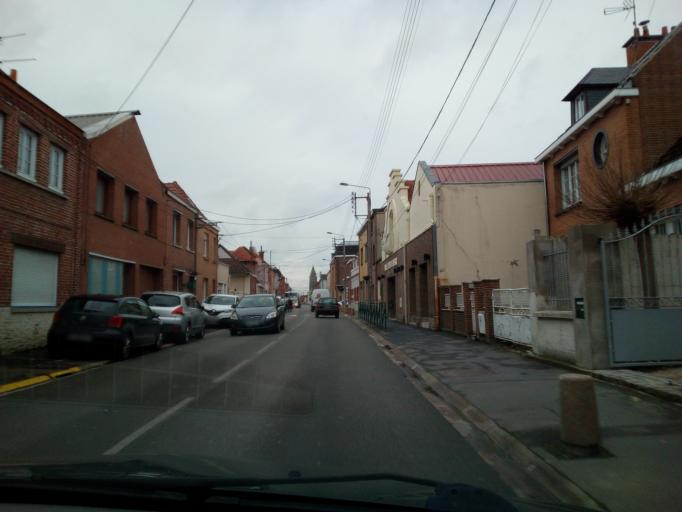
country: FR
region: Nord-Pas-de-Calais
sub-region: Departement du Nord
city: Bauvin
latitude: 50.5139
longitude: 2.8986
